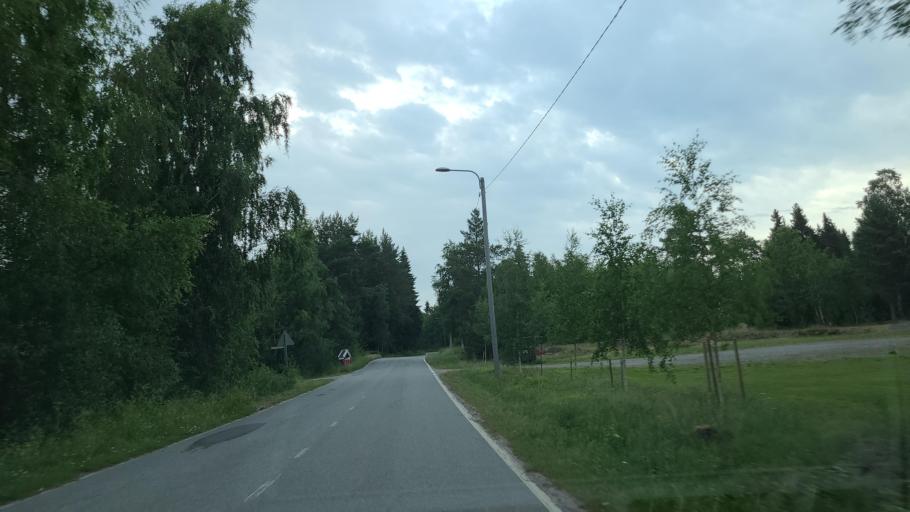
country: FI
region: Ostrobothnia
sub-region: Vaasa
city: Replot
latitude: 63.1725
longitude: 21.2768
